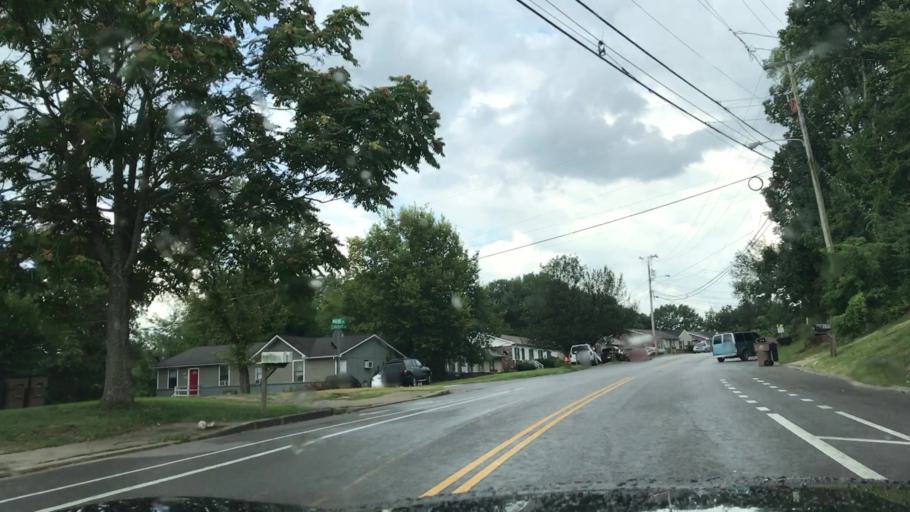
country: US
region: Tennessee
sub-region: Williamson County
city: Brentwood Estates
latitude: 36.0370
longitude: -86.7061
